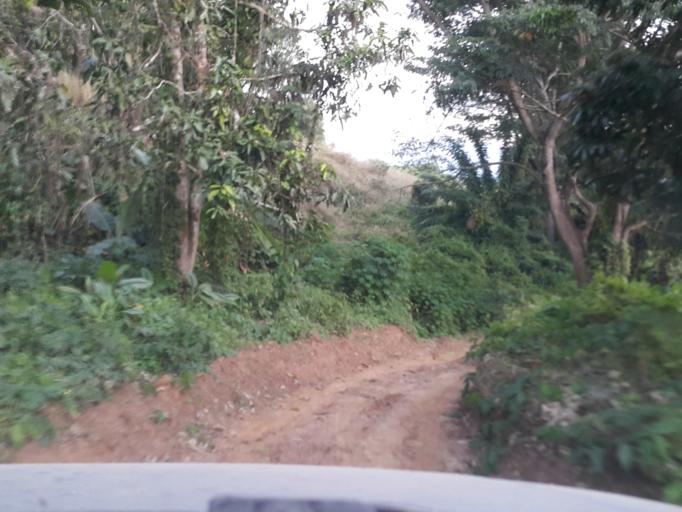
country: TH
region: Lamphun
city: Ban Thi
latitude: 18.5719
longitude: 99.2436
